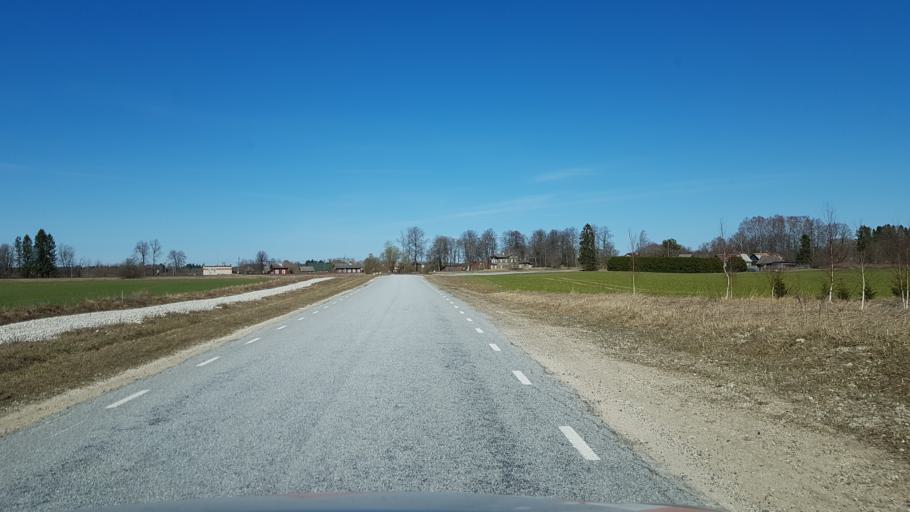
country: EE
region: Laeaene-Virumaa
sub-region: Viru-Nigula vald
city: Kunda
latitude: 59.3420
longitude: 26.6699
